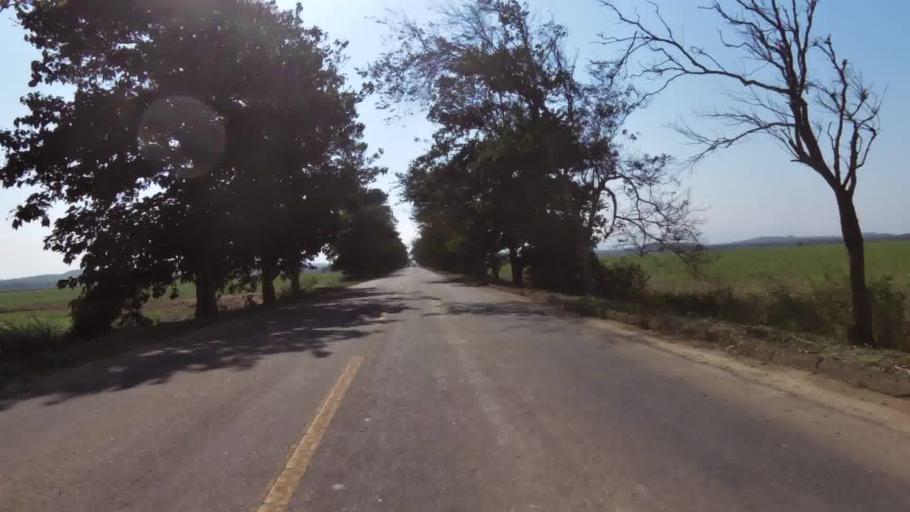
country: BR
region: Espirito Santo
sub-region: Itapemirim
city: Itapemirim
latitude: -20.9928
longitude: -40.8518
